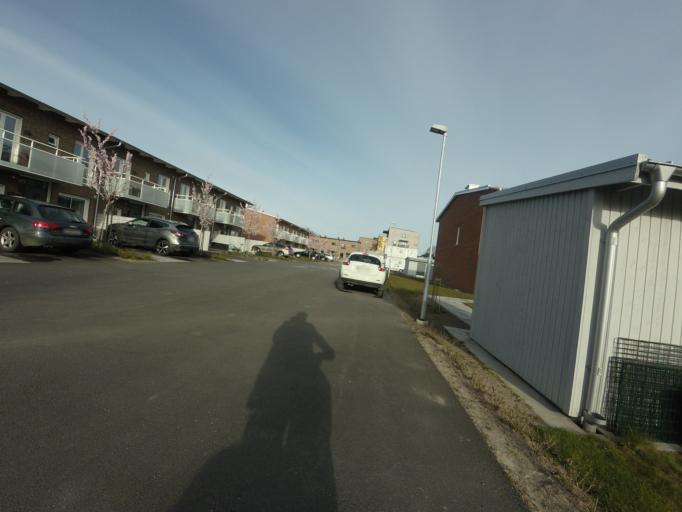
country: SE
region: Skane
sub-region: Hoganas Kommun
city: Hoganas
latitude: 56.1958
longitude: 12.5610
